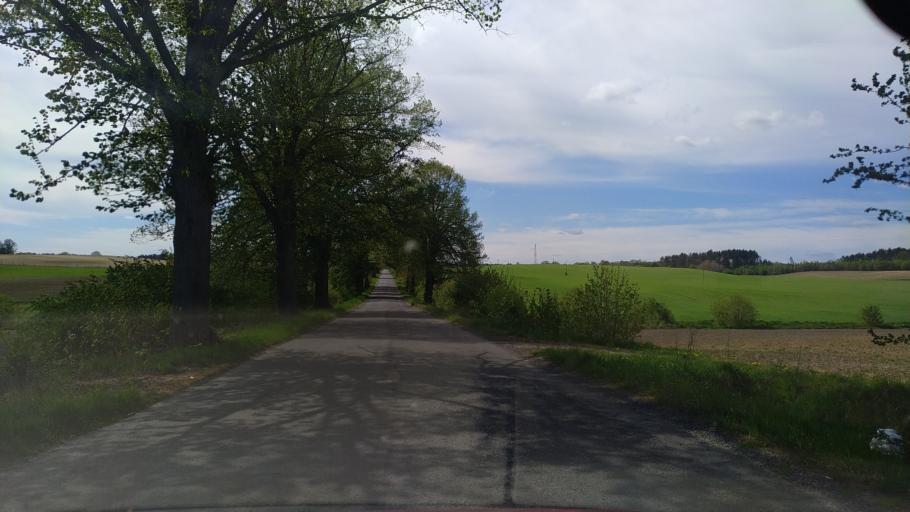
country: PL
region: West Pomeranian Voivodeship
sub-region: Powiat walecki
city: Walcz
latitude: 53.3540
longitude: 16.3050
